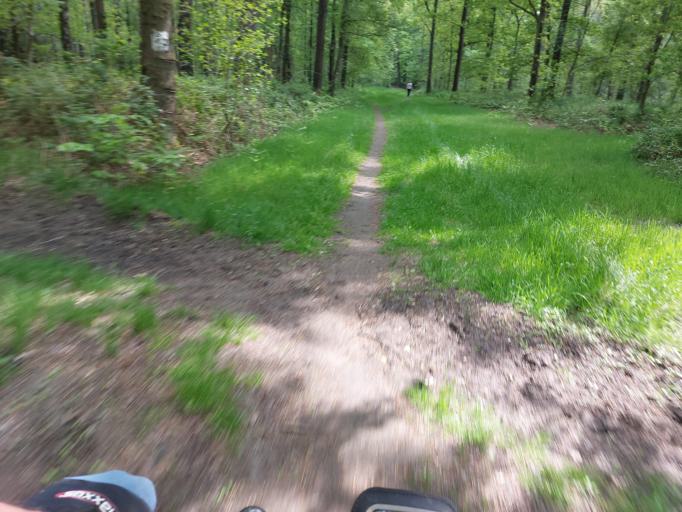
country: BE
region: Wallonia
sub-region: Province du Hainaut
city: Jurbise
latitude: 50.5037
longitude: 3.8527
